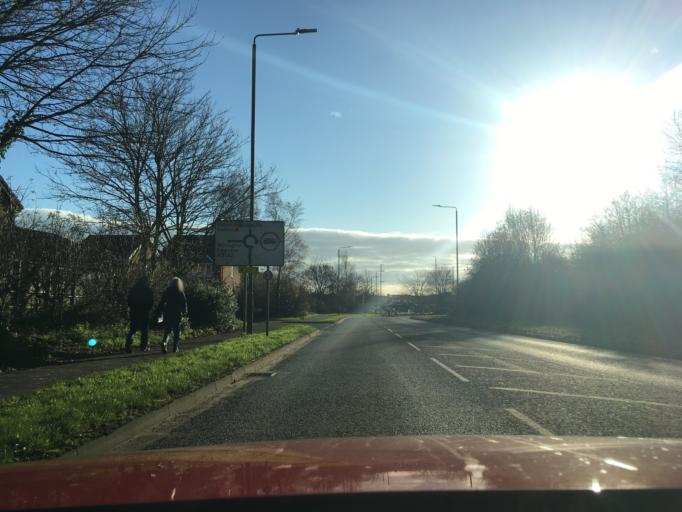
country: GB
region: England
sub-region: Derbyshire
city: Etwall
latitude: 52.8733
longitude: -1.6280
